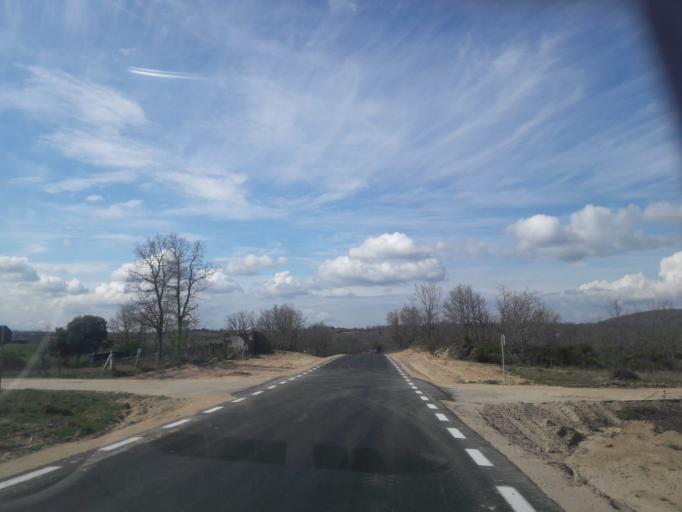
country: ES
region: Castille and Leon
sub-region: Provincia de Salamanca
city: Valdefuentes de Sangusin
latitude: 40.5215
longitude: -5.8452
